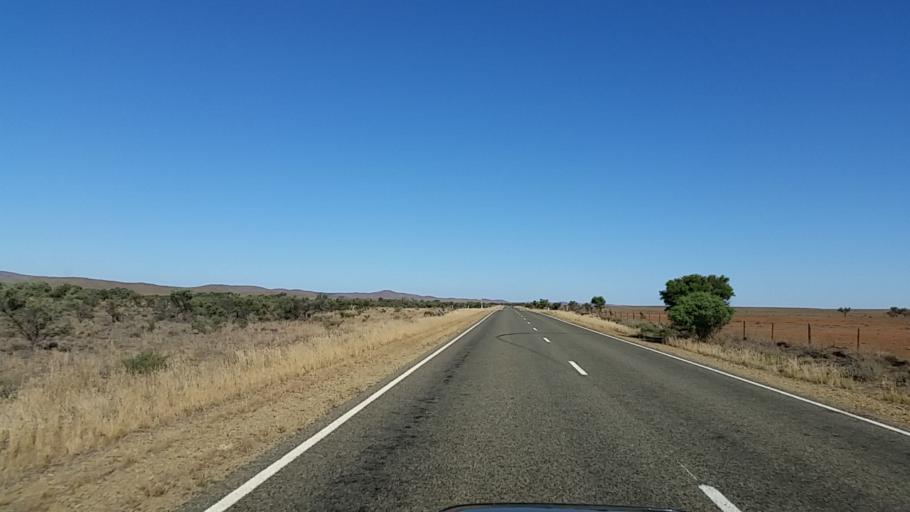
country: AU
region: South Australia
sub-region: Flinders Ranges
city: Quorn
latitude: -32.3975
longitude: 138.5122
